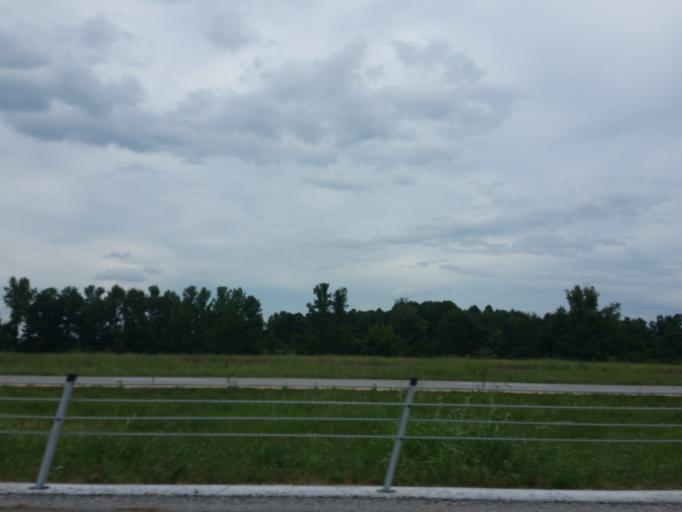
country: US
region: Kentucky
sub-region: Trigg County
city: Cadiz
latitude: 36.9764
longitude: -87.9007
